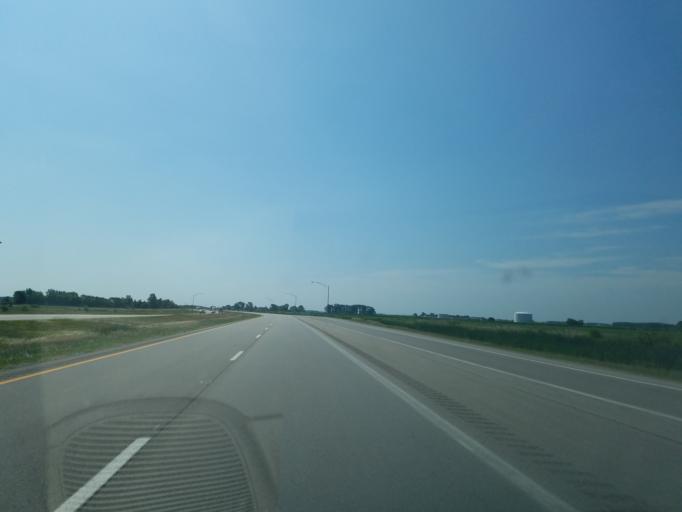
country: US
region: Ohio
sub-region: Van Wert County
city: Van Wert
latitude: 40.8770
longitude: -84.5231
